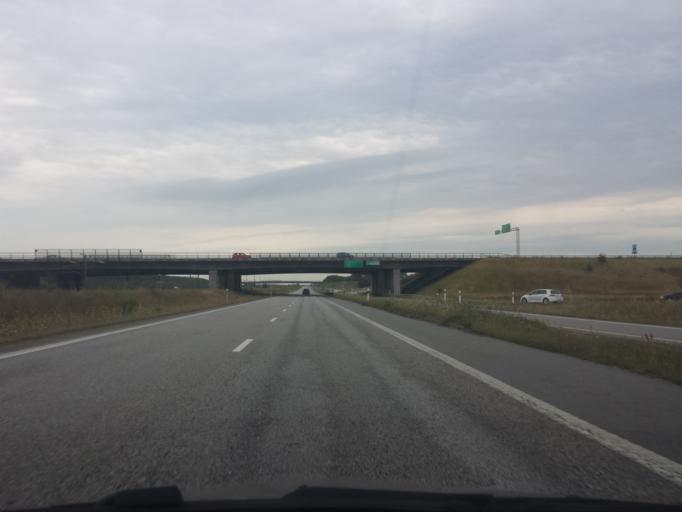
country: SE
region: Skane
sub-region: Malmo
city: Tygelsjo
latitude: 55.5471
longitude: 13.0001
